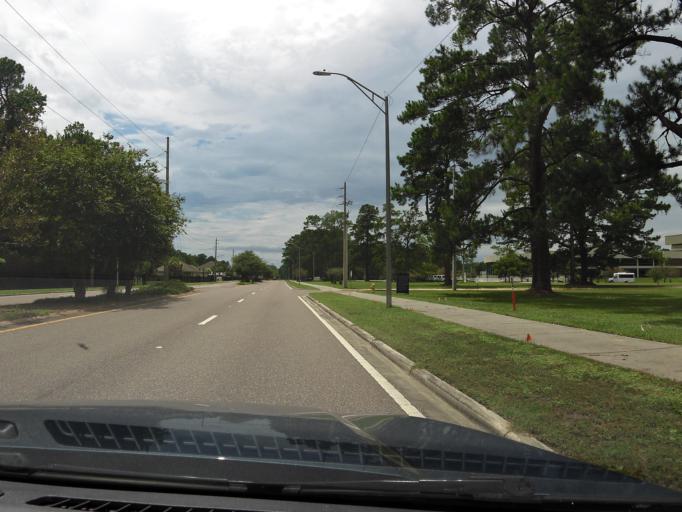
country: US
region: Florida
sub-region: Duval County
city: Jacksonville
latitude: 30.4275
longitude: -81.7158
